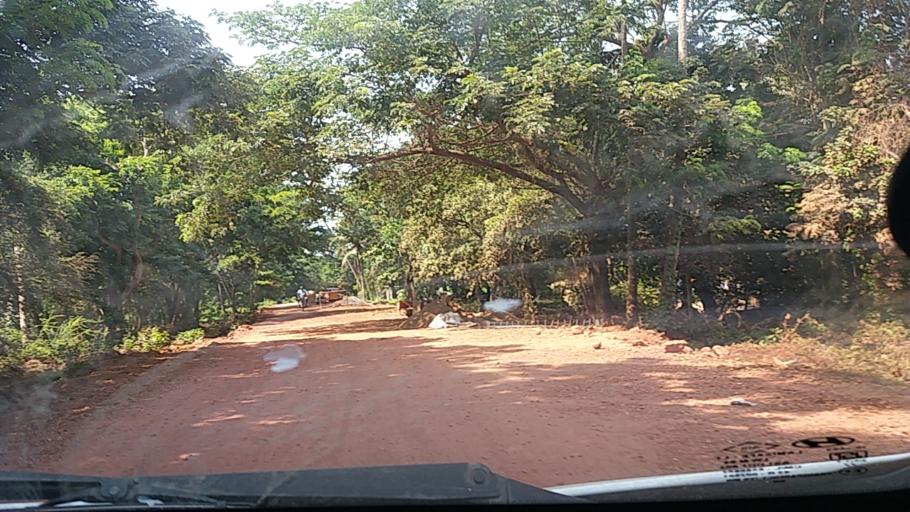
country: IN
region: Goa
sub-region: South Goa
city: Madgaon
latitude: 15.2764
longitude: 73.9527
